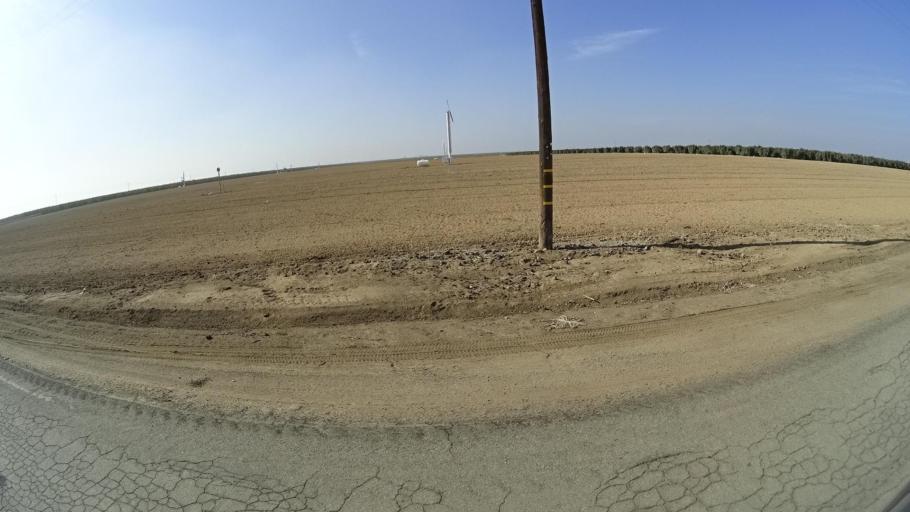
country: US
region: California
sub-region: Kern County
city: Shafter
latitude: 35.5322
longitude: -119.1336
